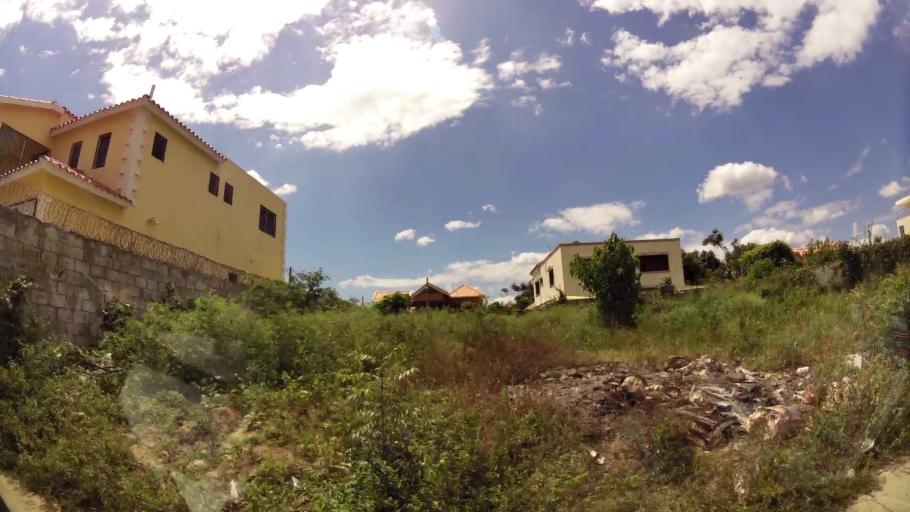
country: DO
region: San Cristobal
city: San Cristobal
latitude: 18.4170
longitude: -70.1016
